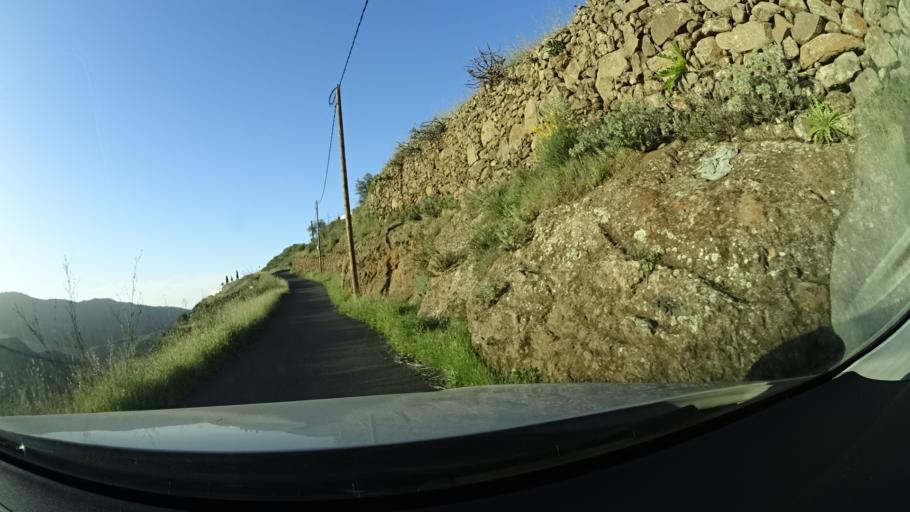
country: ES
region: Canary Islands
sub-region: Provincia de Las Palmas
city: Artenara
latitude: 28.0369
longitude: -15.6461
